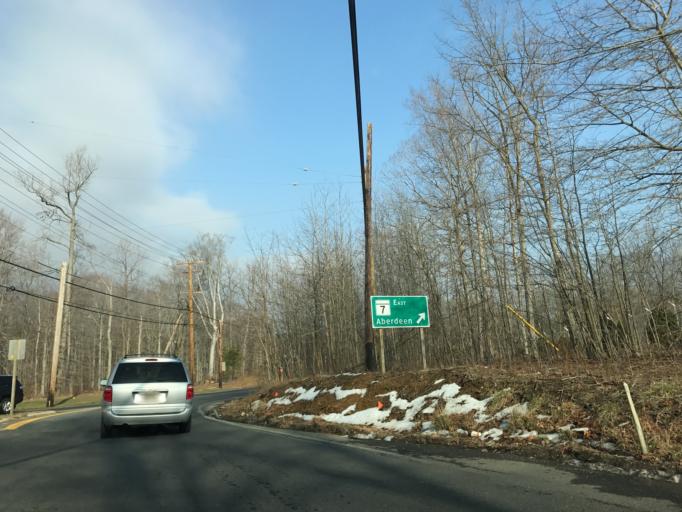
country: US
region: Maryland
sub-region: Harford County
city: Perryman
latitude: 39.4884
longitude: -76.2167
